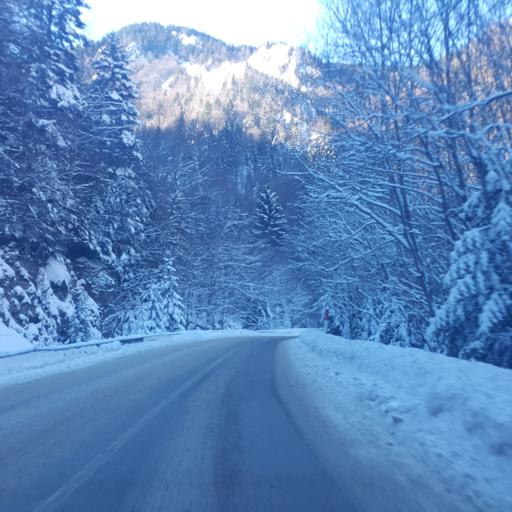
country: XK
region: Mitrovica
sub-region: Komuna e Leposaviqit
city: Leposaviq
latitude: 43.3051
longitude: 20.8593
